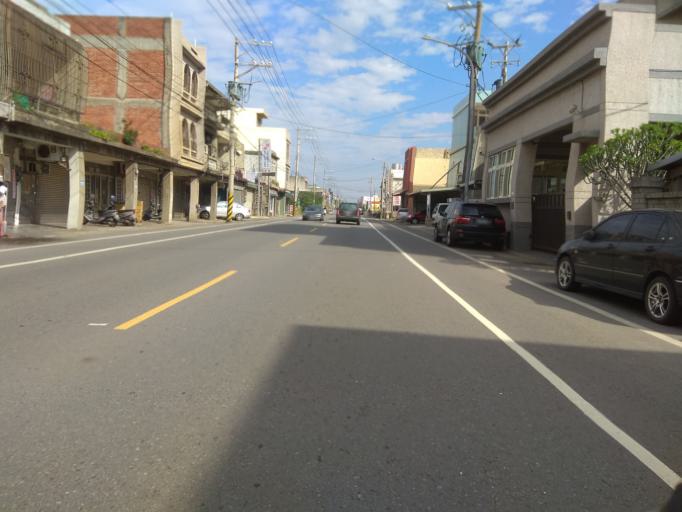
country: TW
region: Taiwan
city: Taoyuan City
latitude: 25.0656
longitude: 121.1881
